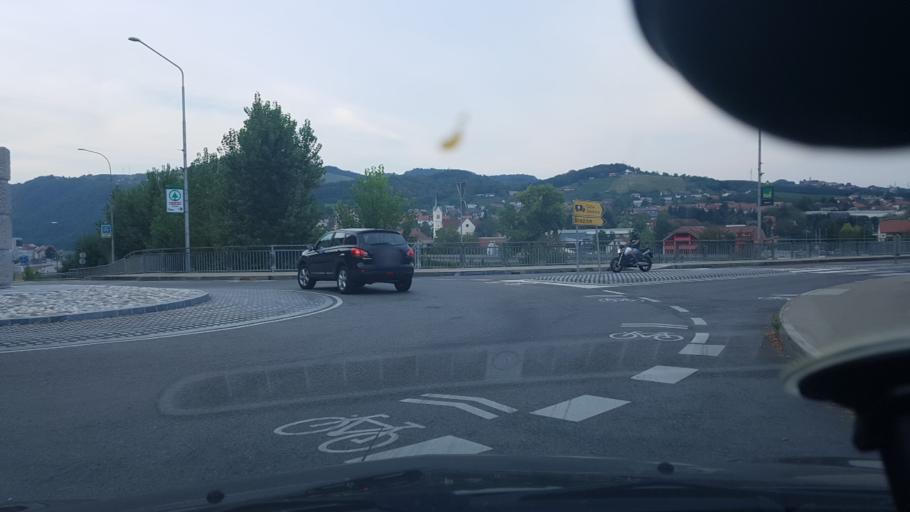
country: SI
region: Krsko
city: Krsko
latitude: 45.9565
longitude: 15.4865
